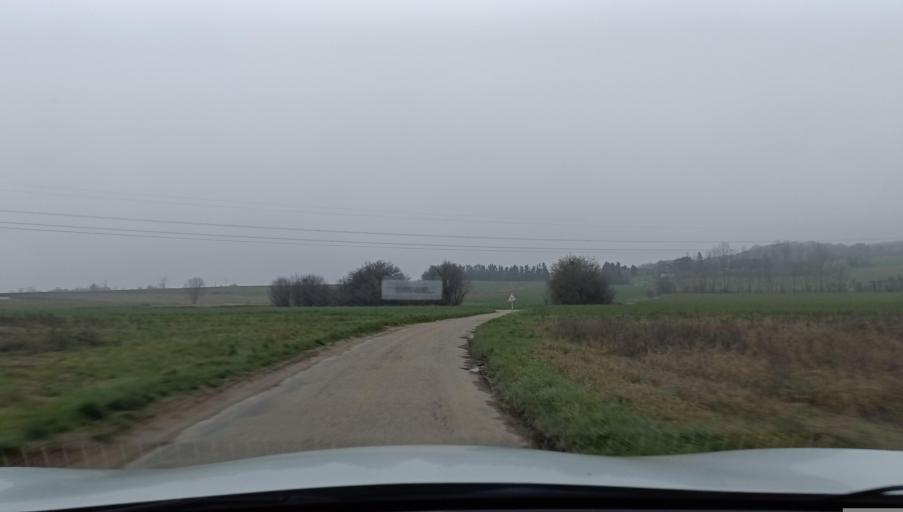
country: FR
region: Rhone-Alpes
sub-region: Departement de l'Isere
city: Seyssuel
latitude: 45.5788
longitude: 4.8491
